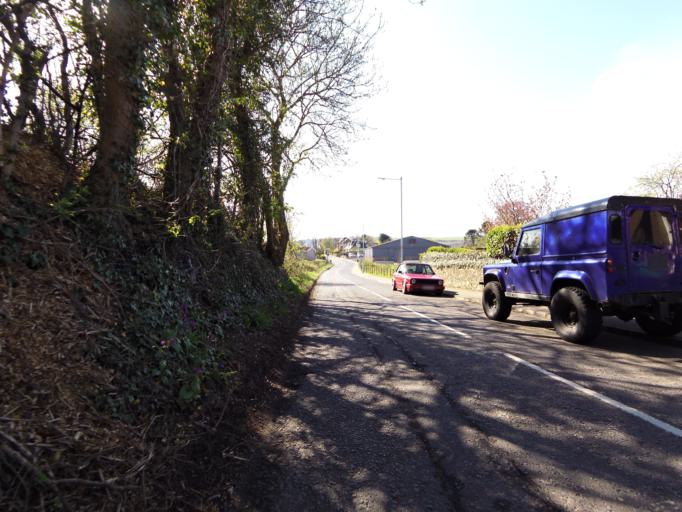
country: GB
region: Scotland
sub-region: Fife
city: Newport-On-Tay
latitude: 56.4213
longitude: -2.9816
